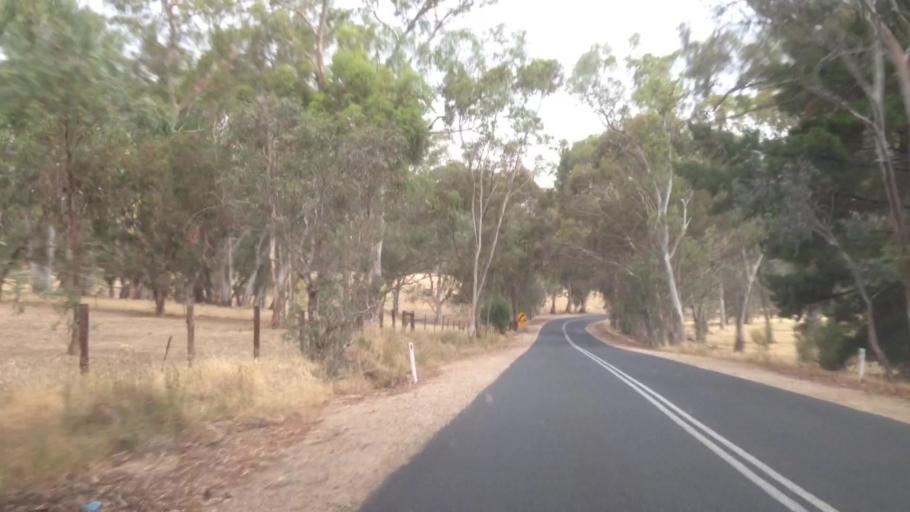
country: AU
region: South Australia
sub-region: Barossa
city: Williamstown
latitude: -34.6489
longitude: 138.8625
